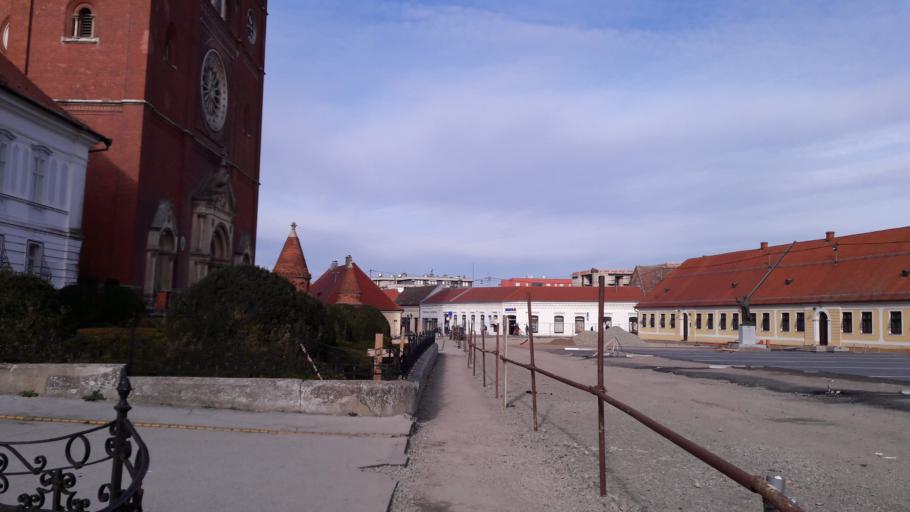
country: HR
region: Osjecko-Baranjska
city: Piskorevci
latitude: 45.3072
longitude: 18.4118
